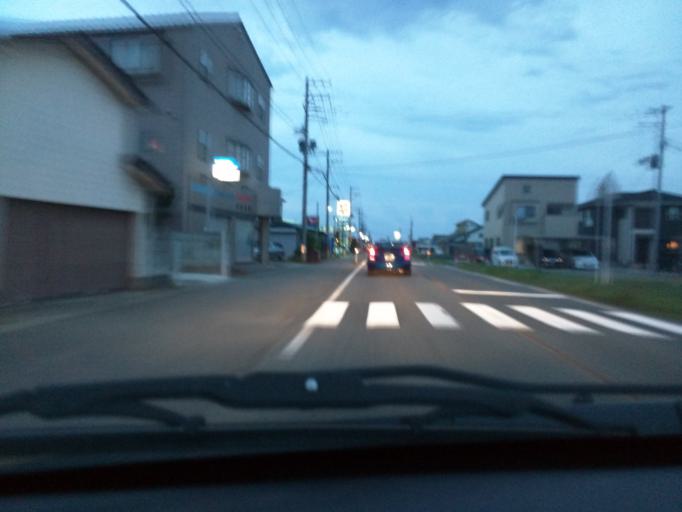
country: JP
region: Niigata
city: Kashiwazaki
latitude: 37.3479
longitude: 138.6088
